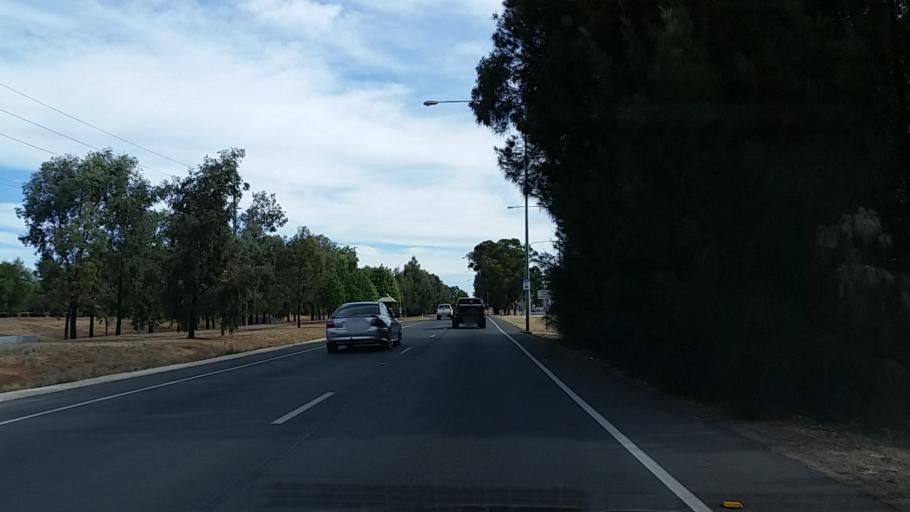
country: AU
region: South Australia
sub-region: Playford
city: Smithfield
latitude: -34.6795
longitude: 138.6961
